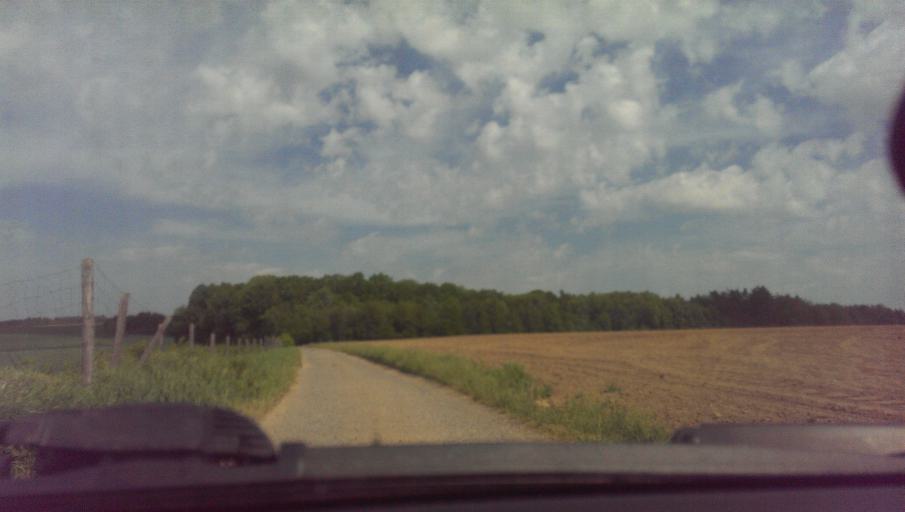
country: CZ
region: Zlin
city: Tlumacov
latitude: 49.2575
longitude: 17.5349
